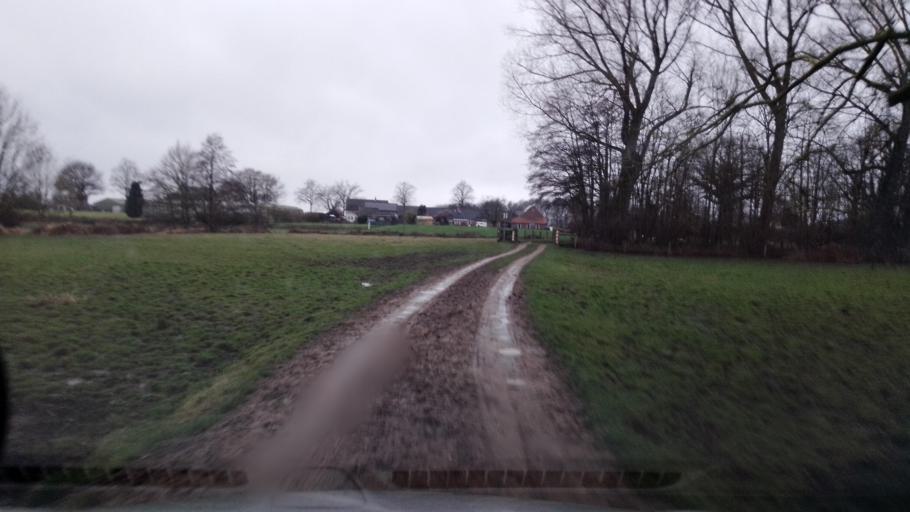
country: NL
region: Limburg
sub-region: Gemeente Venlo
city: Arcen
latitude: 51.4513
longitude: 6.1576
